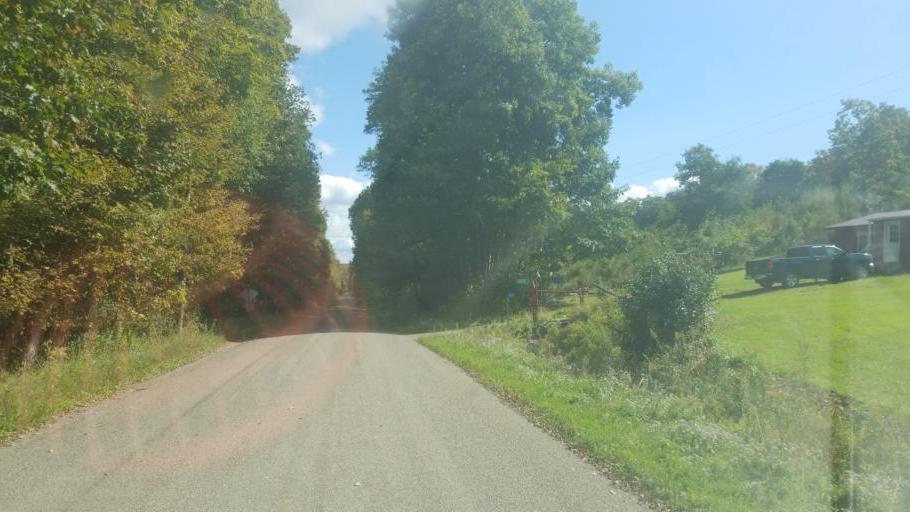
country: US
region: New York
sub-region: Allegany County
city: Cuba
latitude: 42.1929
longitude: -78.3222
